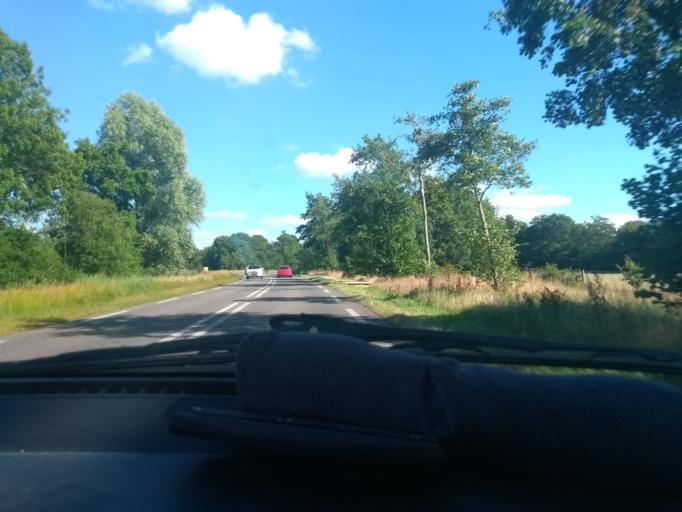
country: NL
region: Groningen
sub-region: Gemeente Leek
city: Leek
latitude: 53.1411
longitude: 6.4834
